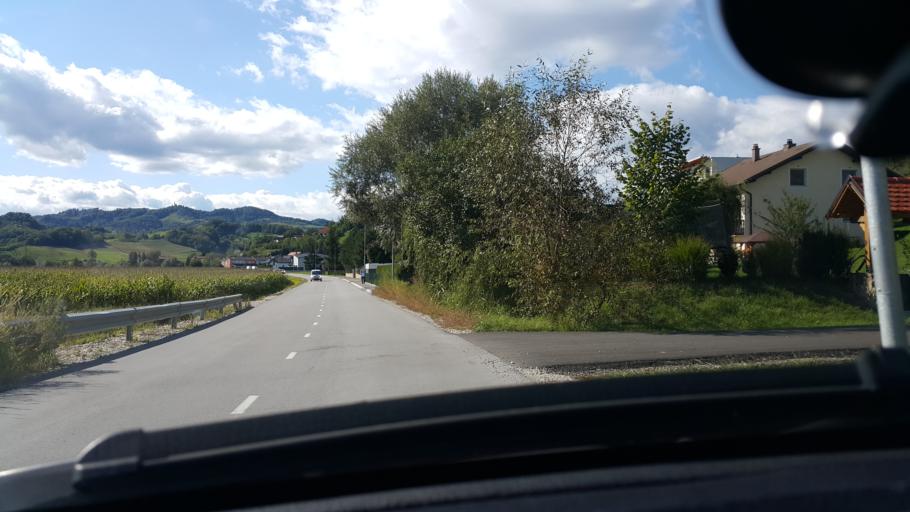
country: SI
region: Pesnica
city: Pesnica pri Mariboru
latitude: 46.6052
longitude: 15.6599
